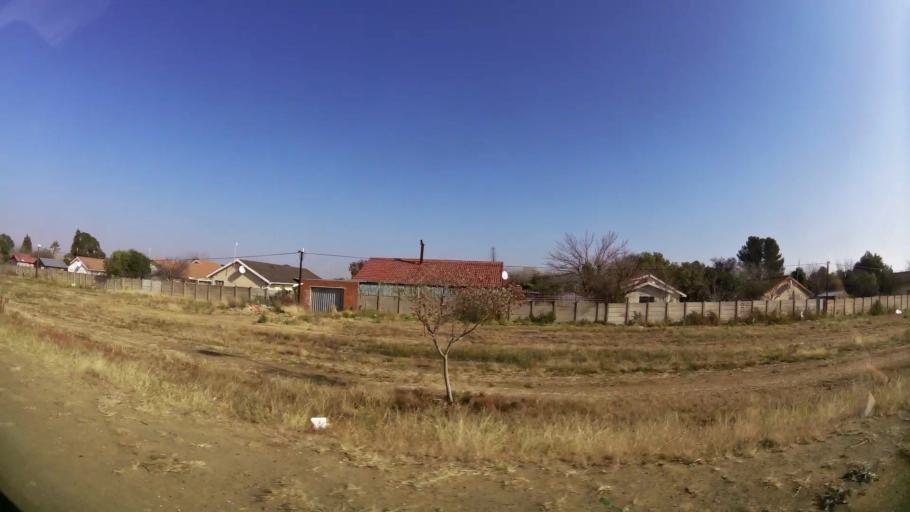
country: ZA
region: Orange Free State
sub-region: Mangaung Metropolitan Municipality
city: Bloemfontein
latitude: -29.1726
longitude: 26.1933
